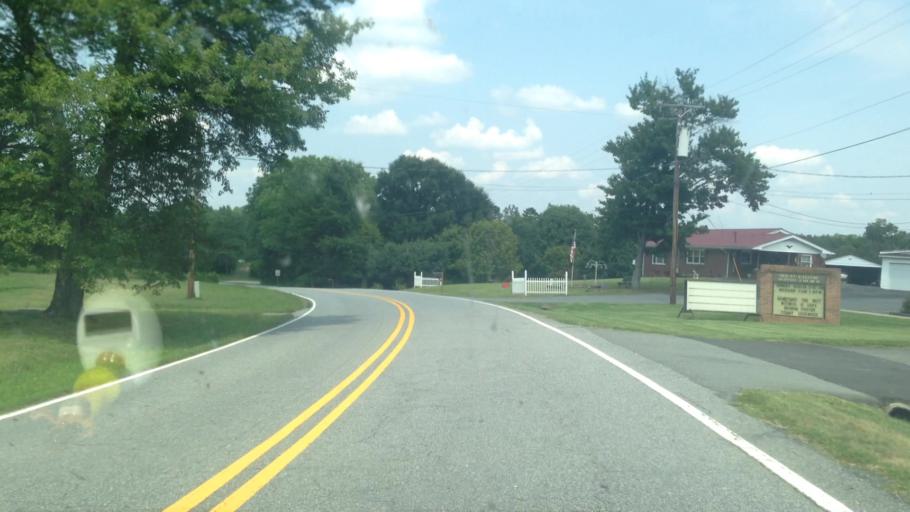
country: US
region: North Carolina
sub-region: Stokes County
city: Walnut Cove
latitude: 36.2419
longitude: -80.1022
